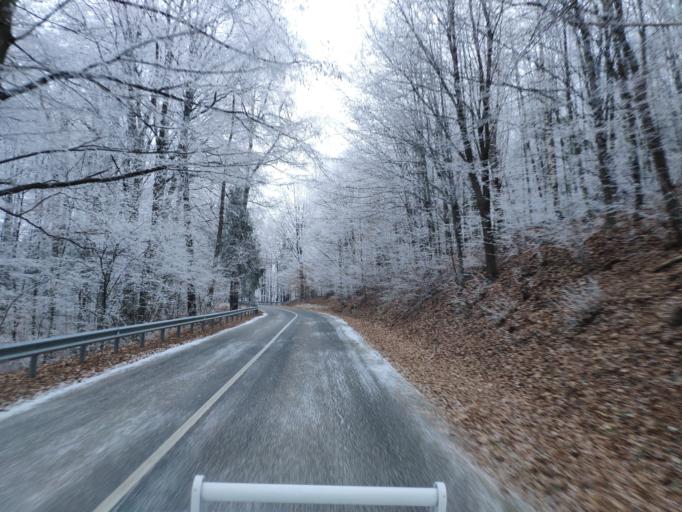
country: SK
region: Kosicky
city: Dobsina
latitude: 48.7971
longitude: 20.4841
